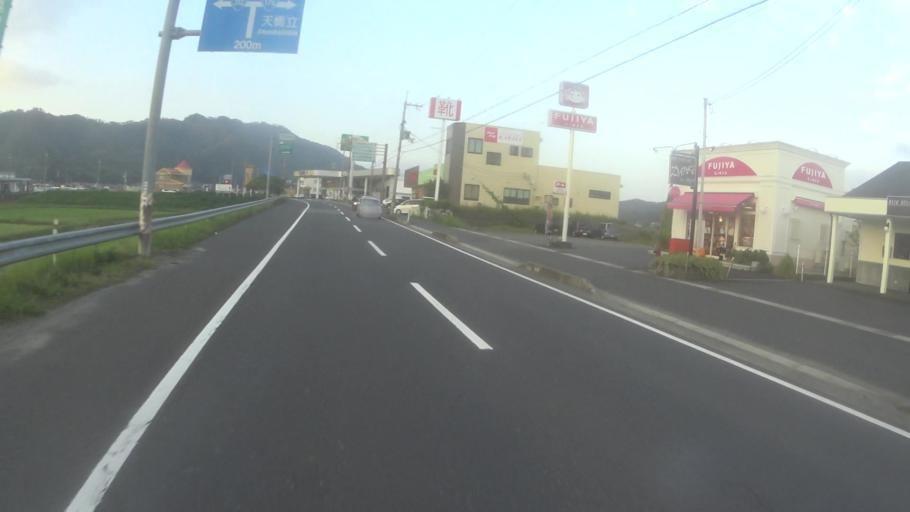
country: JP
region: Kyoto
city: Miyazu
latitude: 35.5328
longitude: 135.1221
